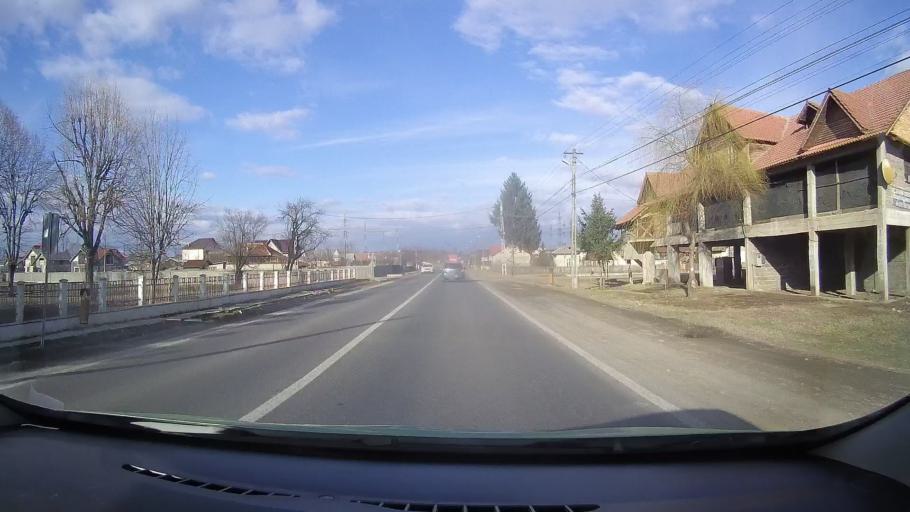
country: RO
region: Dambovita
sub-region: Comuna Ulmi
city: Viisoara
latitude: 44.8803
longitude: 25.4270
